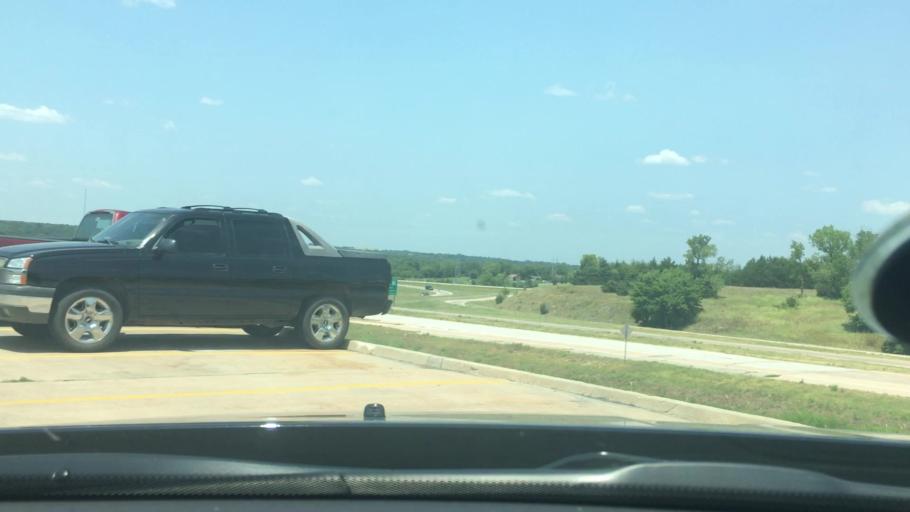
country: US
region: Oklahoma
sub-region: Pontotoc County
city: Ada
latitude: 34.7741
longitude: -96.6986
